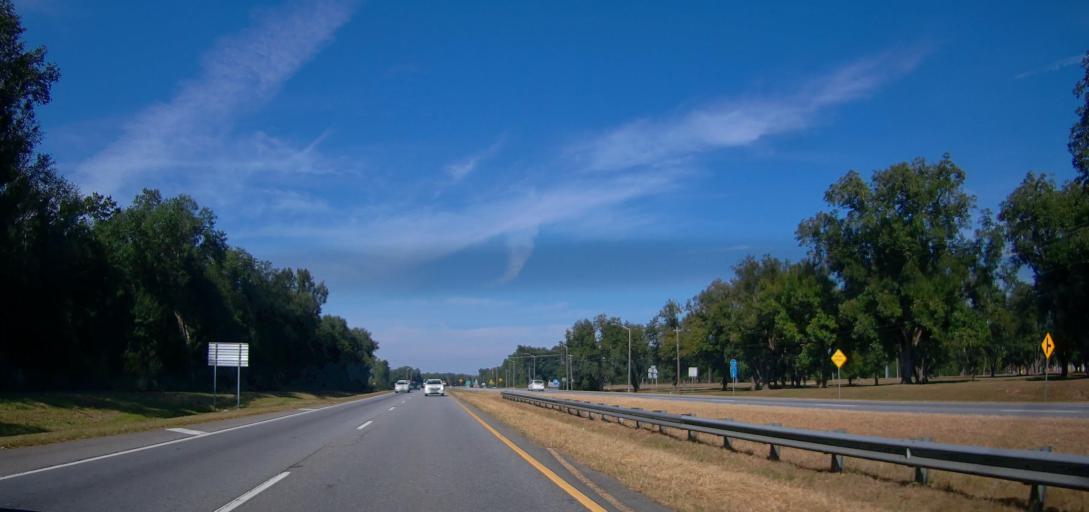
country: US
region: Georgia
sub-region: Dougherty County
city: Albany
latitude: 31.5506
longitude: -84.1151
